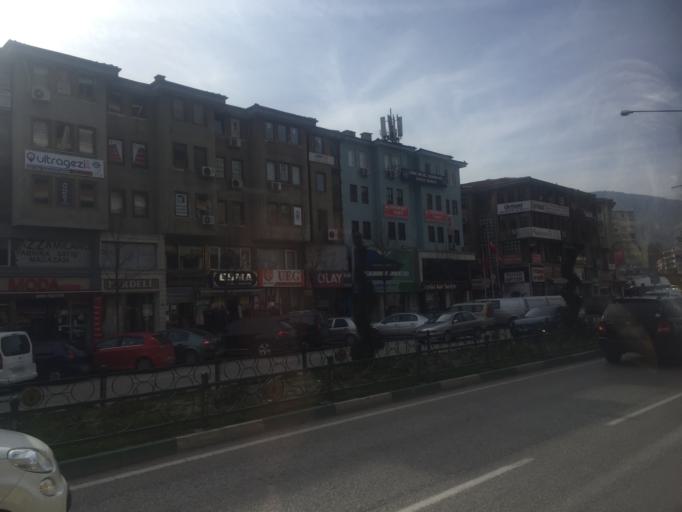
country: TR
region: Bursa
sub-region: Osmangazi
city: Bursa
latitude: 40.1883
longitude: 29.0636
